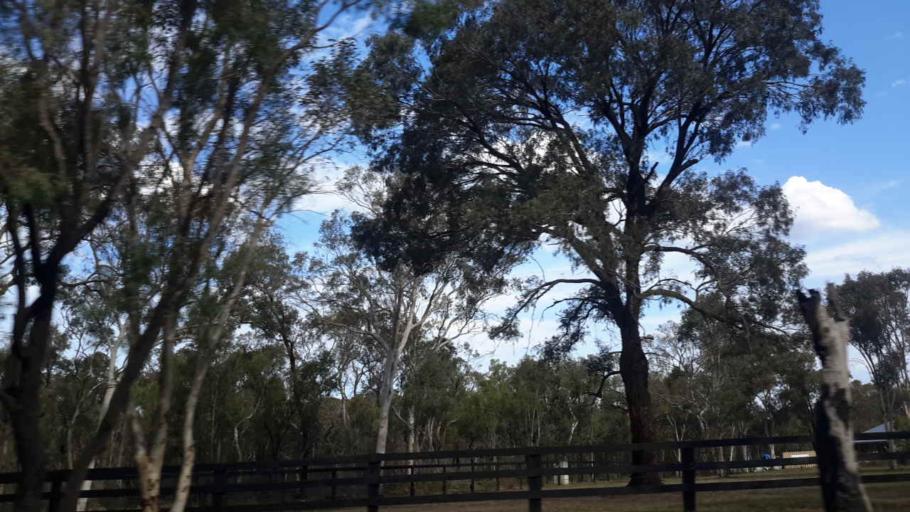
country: AU
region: New South Wales
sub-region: Penrith Municipality
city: Werrington Downs
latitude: -33.6831
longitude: 150.7390
